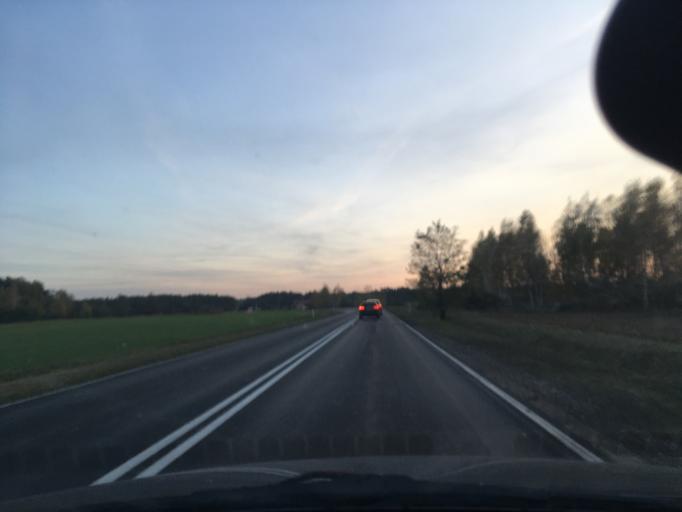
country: PL
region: Masovian Voivodeship
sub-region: Powiat plocki
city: Wyszogrod
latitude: 52.3539
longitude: 20.2091
